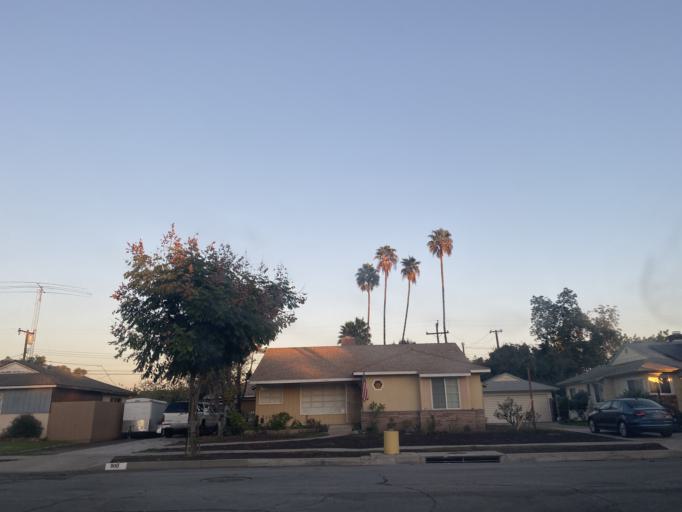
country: US
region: California
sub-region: Orange County
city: Fullerton
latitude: 33.8785
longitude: -117.9037
